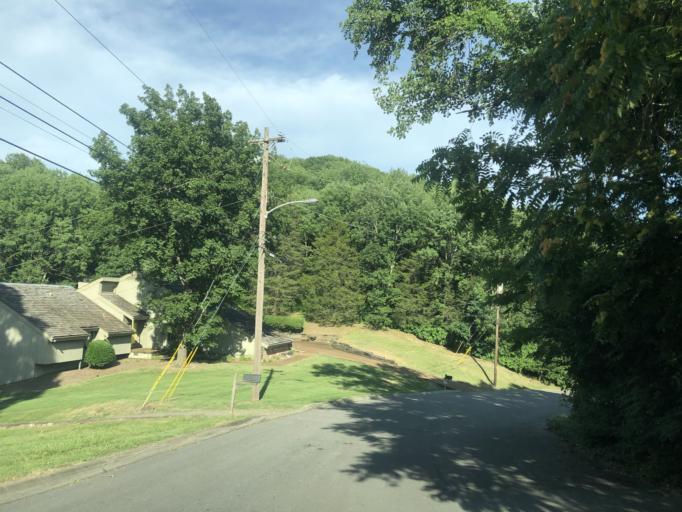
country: US
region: Tennessee
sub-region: Davidson County
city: Nashville
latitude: 36.2245
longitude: -86.8350
